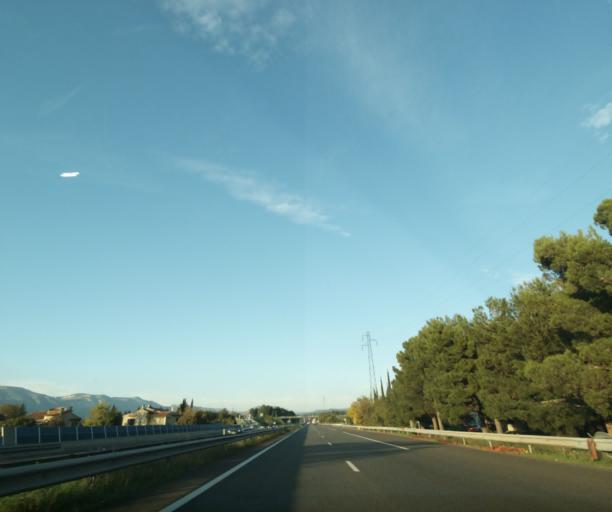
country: FR
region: Provence-Alpes-Cote d'Azur
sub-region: Departement des Bouches-du-Rhone
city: Aubagne
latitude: 43.2946
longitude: 5.5884
